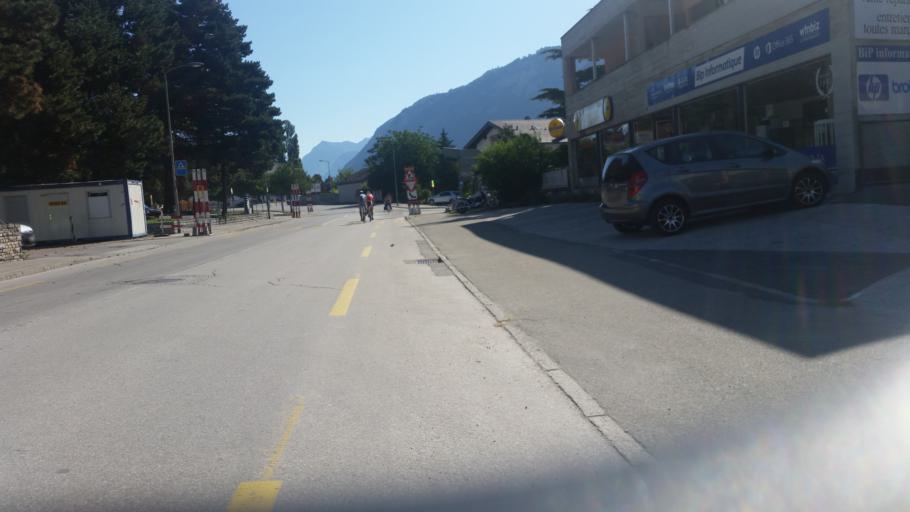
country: CH
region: Valais
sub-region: Sion District
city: Sitten
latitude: 46.2275
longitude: 7.3665
